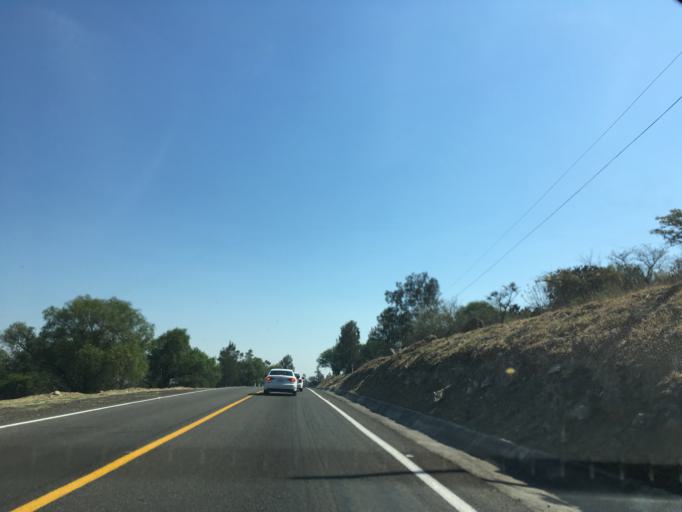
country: MX
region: Michoacan
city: Charo
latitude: 19.7677
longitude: -101.0201
